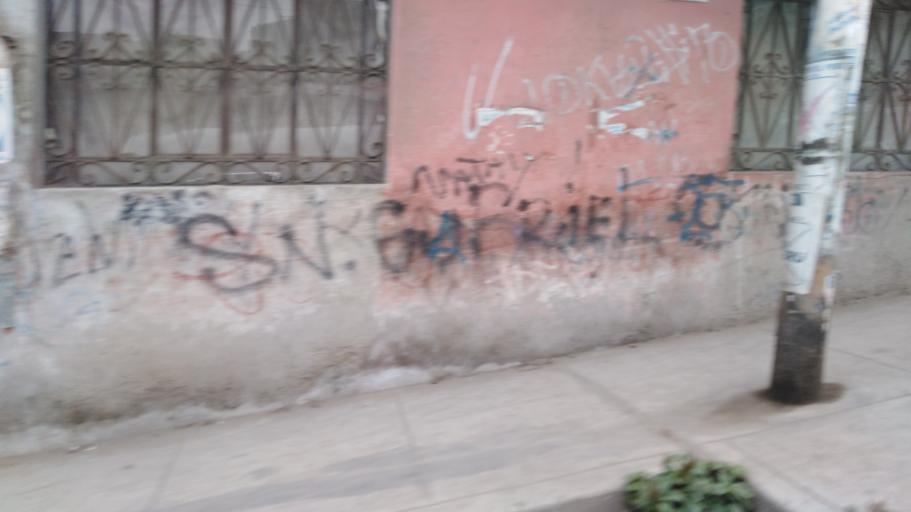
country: PE
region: Lima
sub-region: Lima
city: La Molina
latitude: -12.1428
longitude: -76.9426
